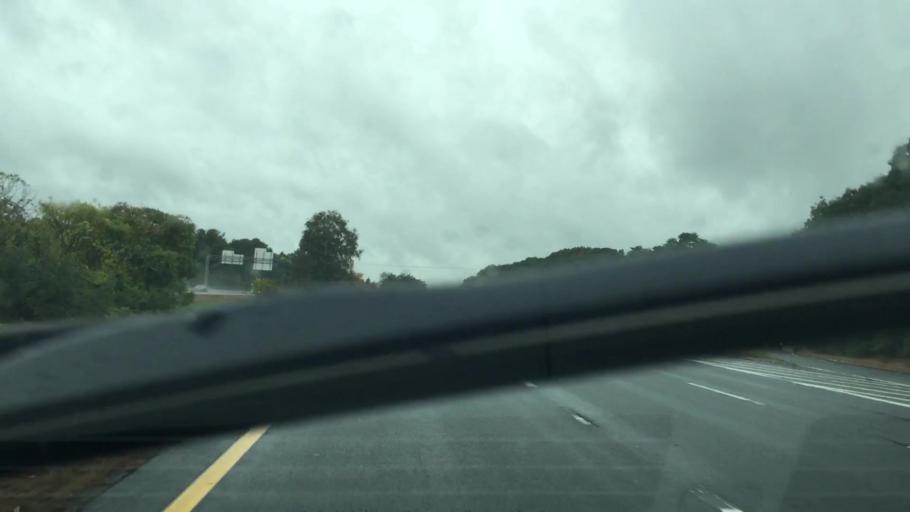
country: US
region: Massachusetts
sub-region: Essex County
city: Amesbury
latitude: 42.8408
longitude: -70.9322
